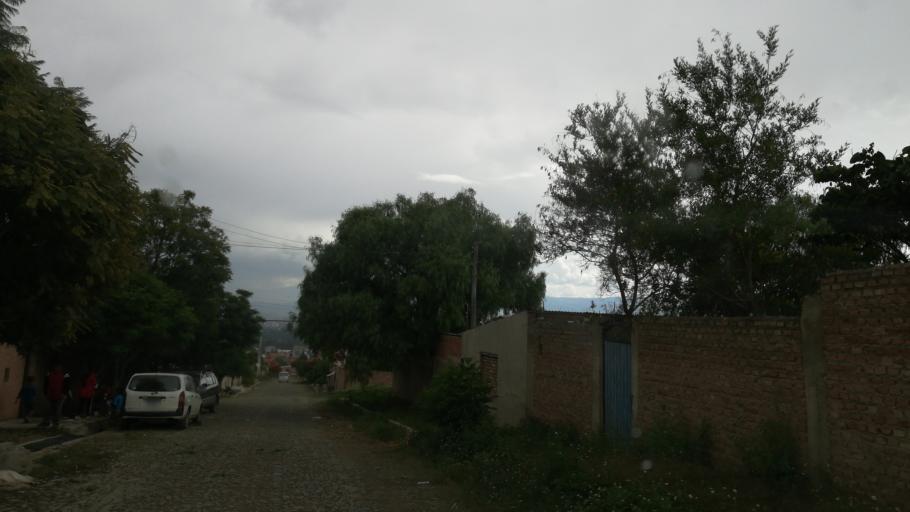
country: BO
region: Cochabamba
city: Cochabamba
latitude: -17.3315
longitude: -66.1945
